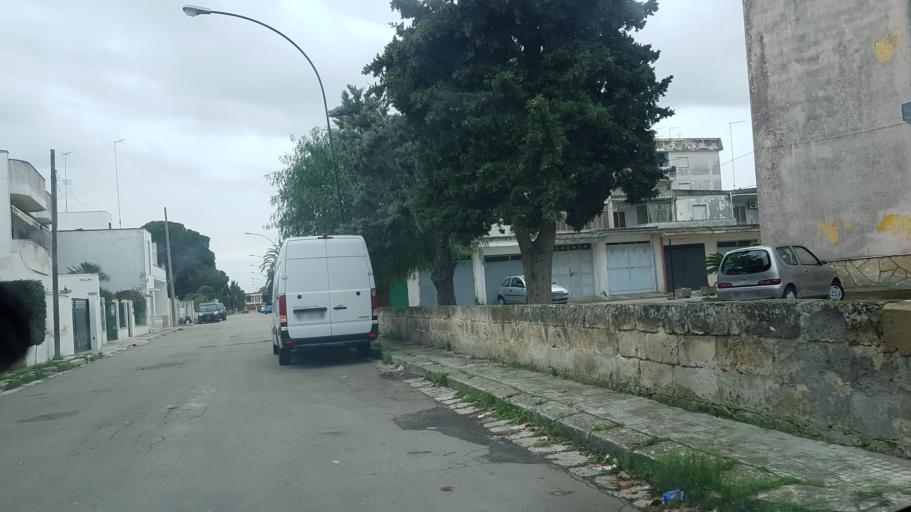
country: IT
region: Apulia
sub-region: Provincia di Lecce
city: Squinzano
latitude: 40.4388
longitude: 18.0358
